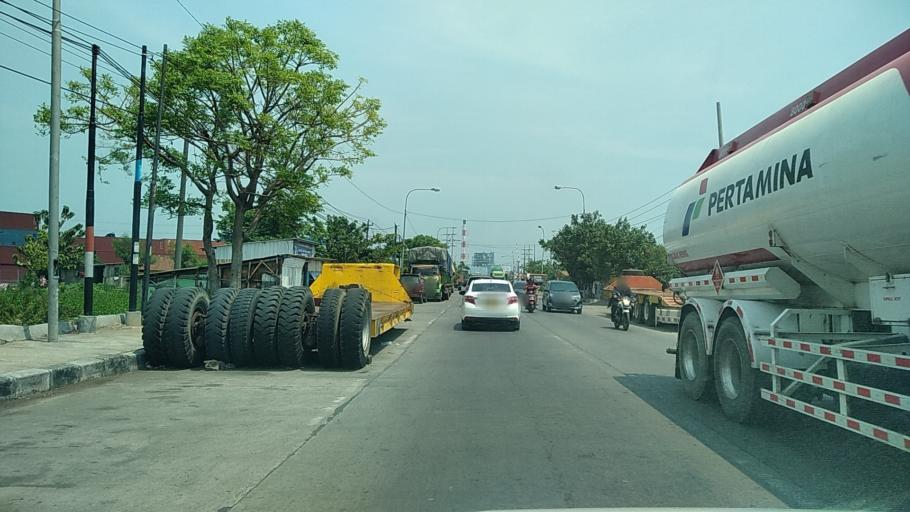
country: ID
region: Central Java
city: Semarang
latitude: -6.9600
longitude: 110.4308
